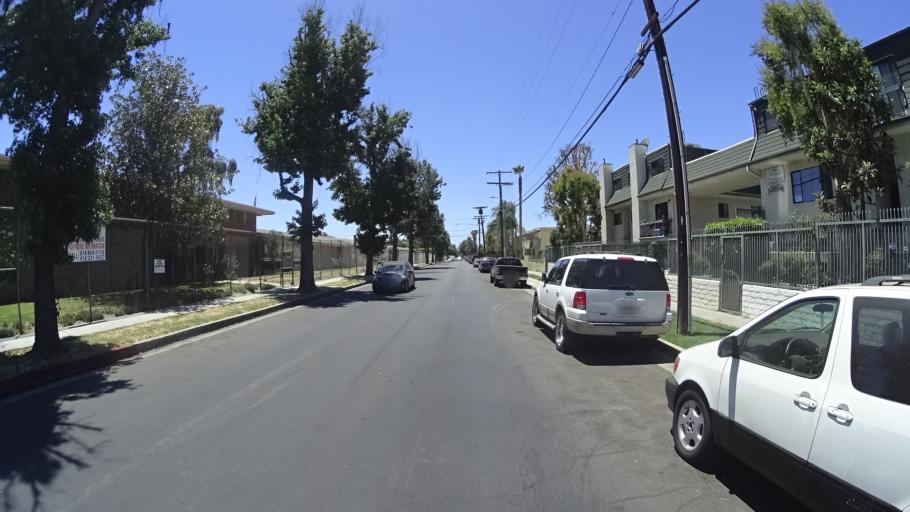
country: US
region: California
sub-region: Los Angeles County
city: Van Nuys
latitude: 34.2349
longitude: -118.4699
